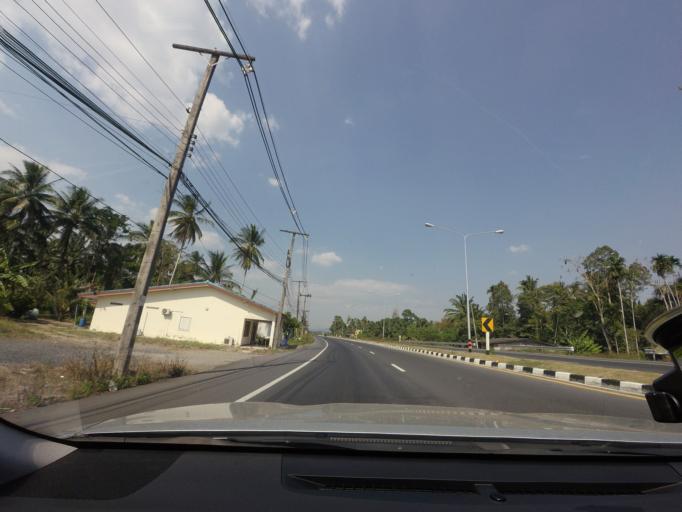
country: TH
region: Phangnga
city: Thap Put
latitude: 8.5433
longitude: 98.7255
